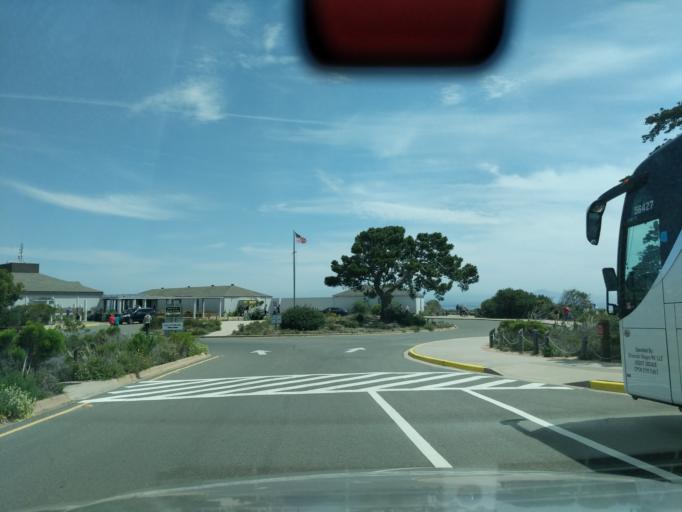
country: US
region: California
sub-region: San Diego County
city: Coronado
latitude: 32.6739
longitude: -117.2403
